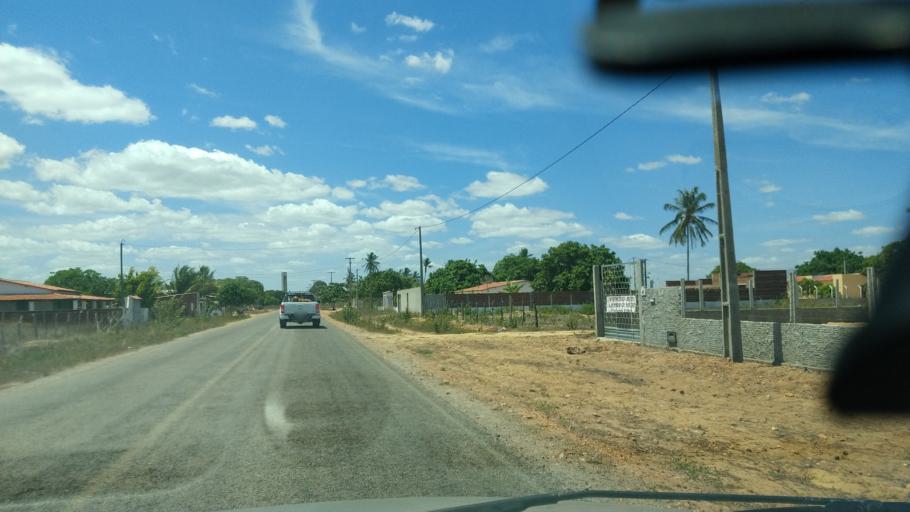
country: BR
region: Rio Grande do Norte
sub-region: Sao Paulo Do Potengi
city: Sao Paulo do Potengi
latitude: -5.9162
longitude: -35.7235
